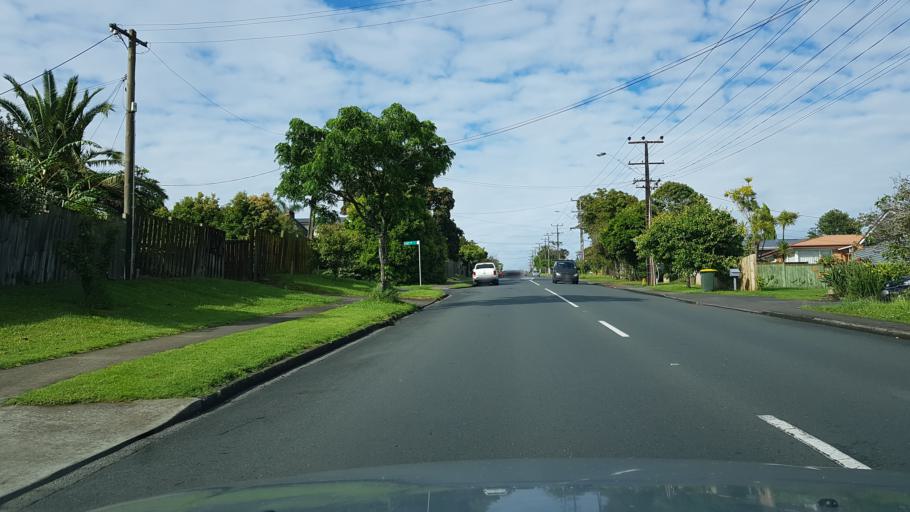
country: NZ
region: Auckland
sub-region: Auckland
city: North Shore
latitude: -36.7963
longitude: 174.7425
